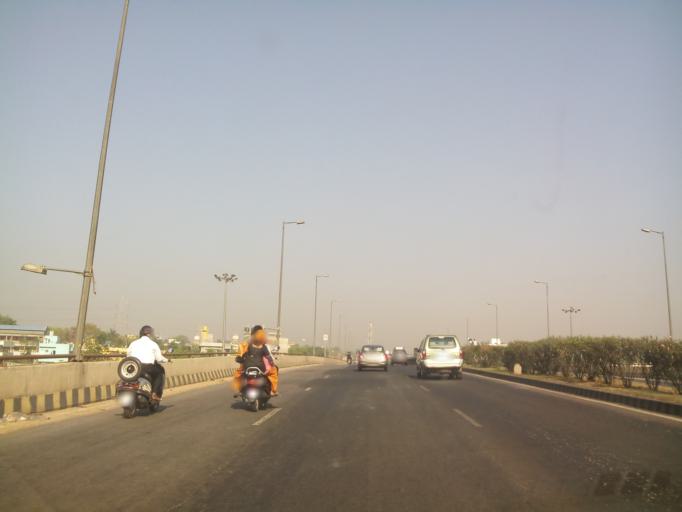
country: IN
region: Karnataka
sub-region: Bangalore Rural
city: Nelamangala
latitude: 13.0923
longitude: 77.3957
